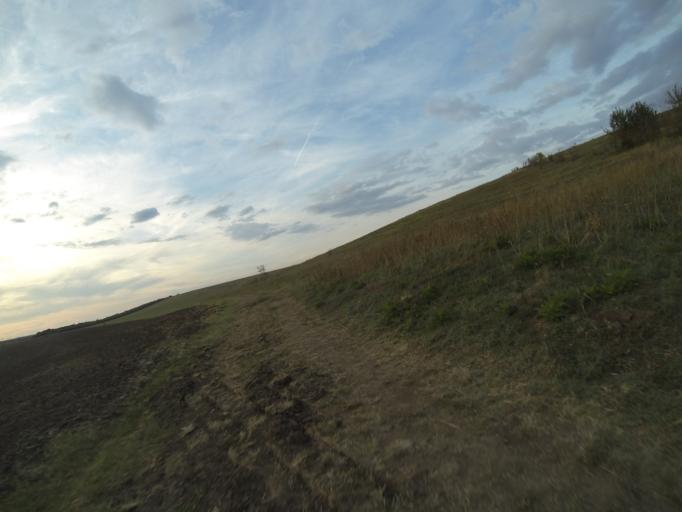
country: RO
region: Dolj
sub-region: Comuna Ceratu
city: Ceratu
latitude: 44.0937
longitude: 23.6665
